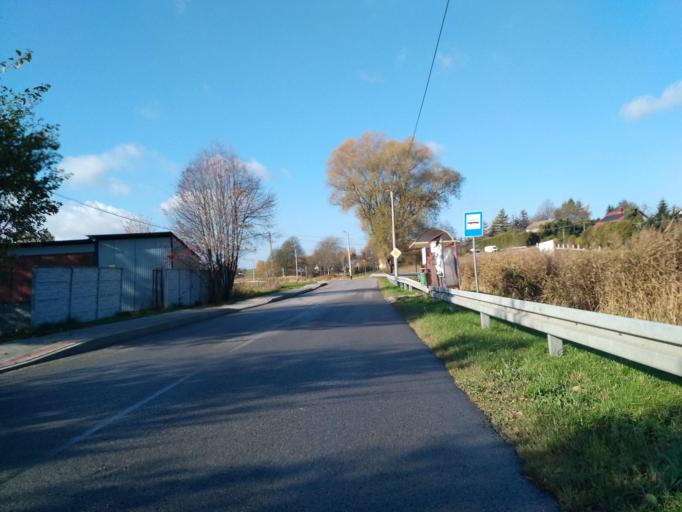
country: PL
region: Subcarpathian Voivodeship
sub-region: Powiat rzeszowski
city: Zglobien
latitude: 50.0334
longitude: 21.8493
